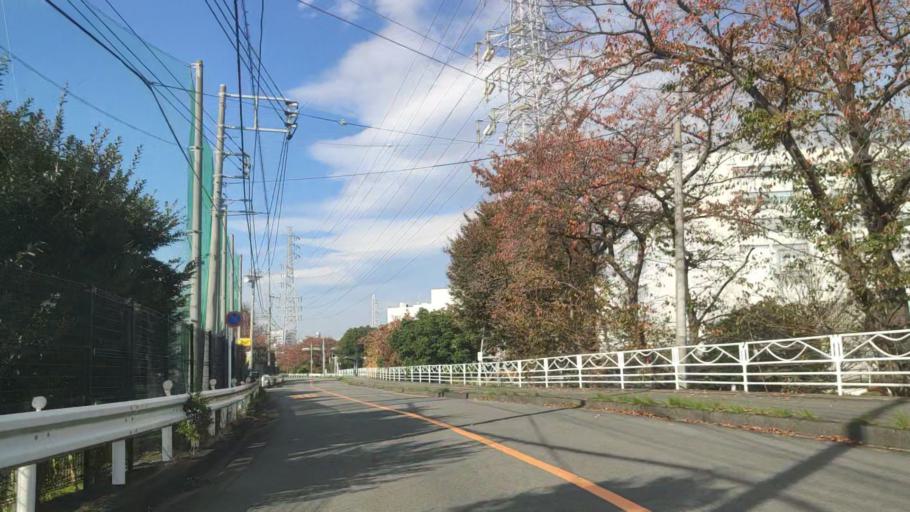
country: JP
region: Kanagawa
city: Atsugi
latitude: 35.4299
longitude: 139.3690
